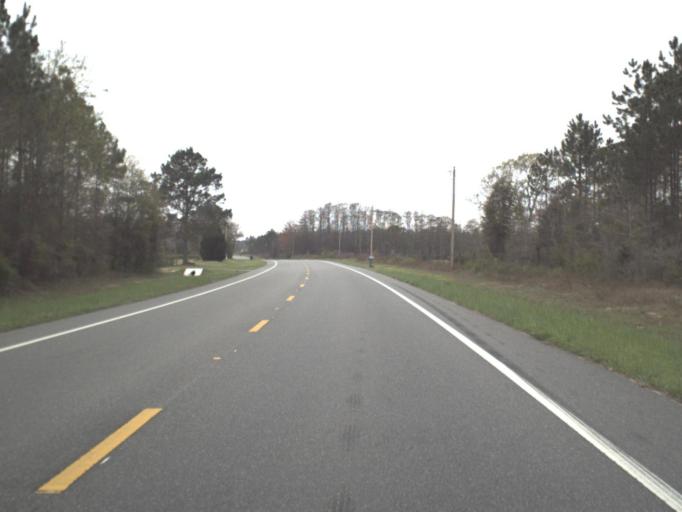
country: US
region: Florida
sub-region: Calhoun County
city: Blountstown
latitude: 30.4124
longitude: -85.2073
